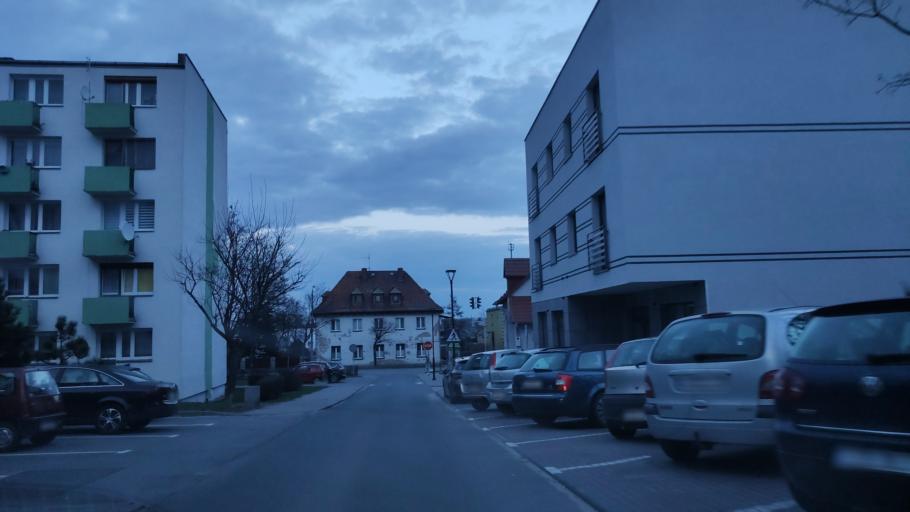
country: PL
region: Kujawsko-Pomorskie
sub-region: Powiat zninski
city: Znin
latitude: 52.8506
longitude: 17.7183
